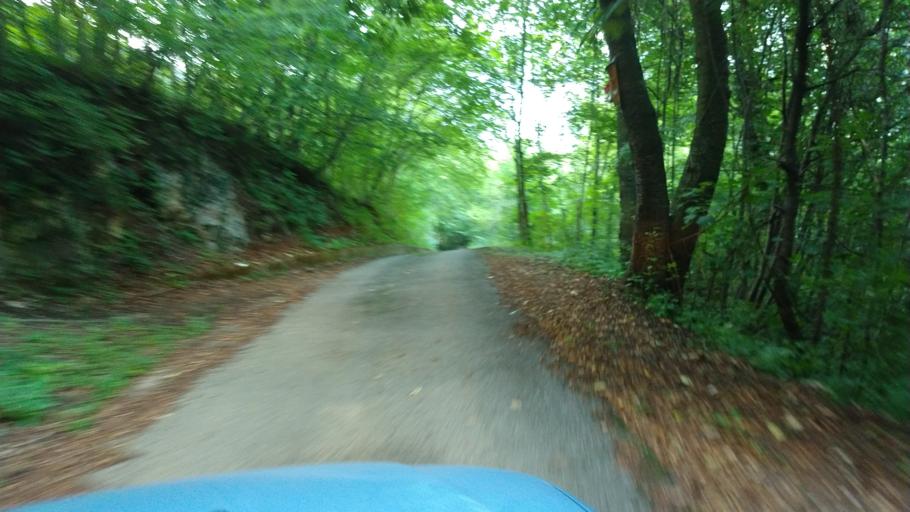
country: IT
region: Veneto
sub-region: Provincia di Vicenza
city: Campolongo sul Brenta
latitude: 45.8242
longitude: 11.6887
